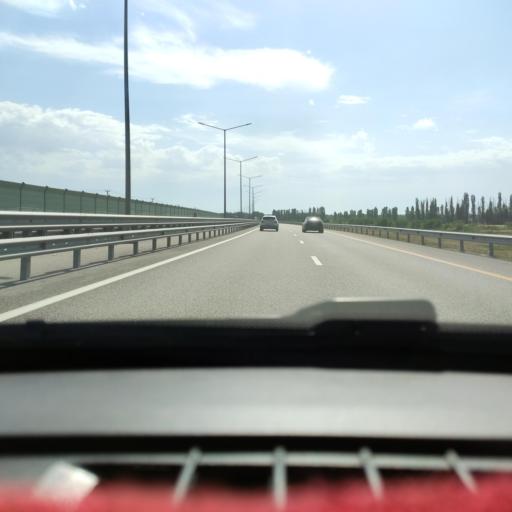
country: RU
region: Voronezj
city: Novaya Usman'
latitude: 51.5907
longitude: 39.3746
